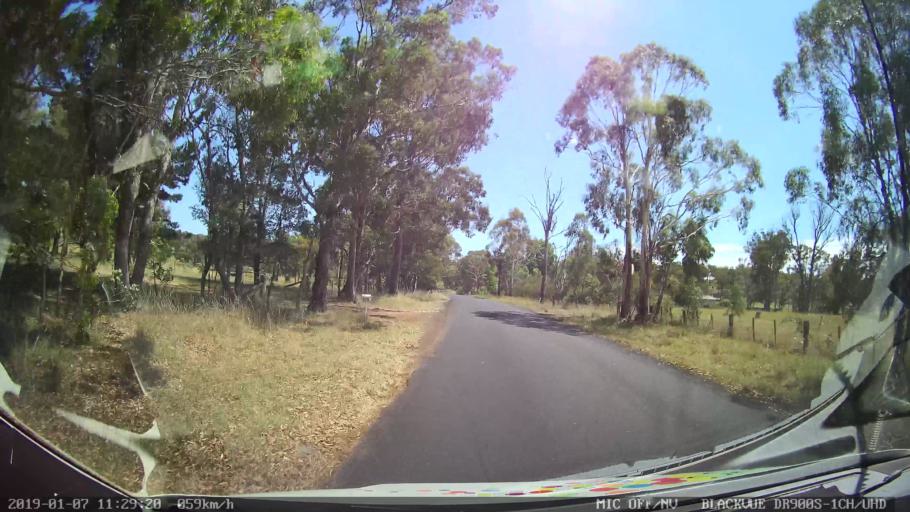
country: AU
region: New South Wales
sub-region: Armidale Dumaresq
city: Armidale
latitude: -30.4398
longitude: 151.5651
